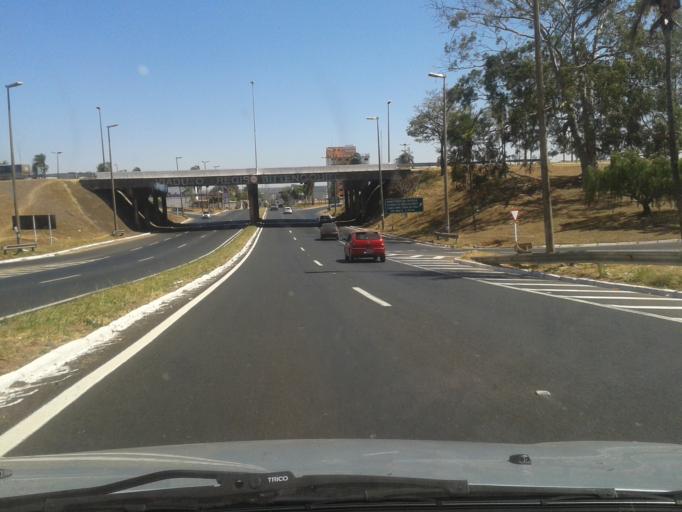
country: BR
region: Minas Gerais
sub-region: Uberlandia
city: Uberlandia
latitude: -18.8849
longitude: -48.2651
